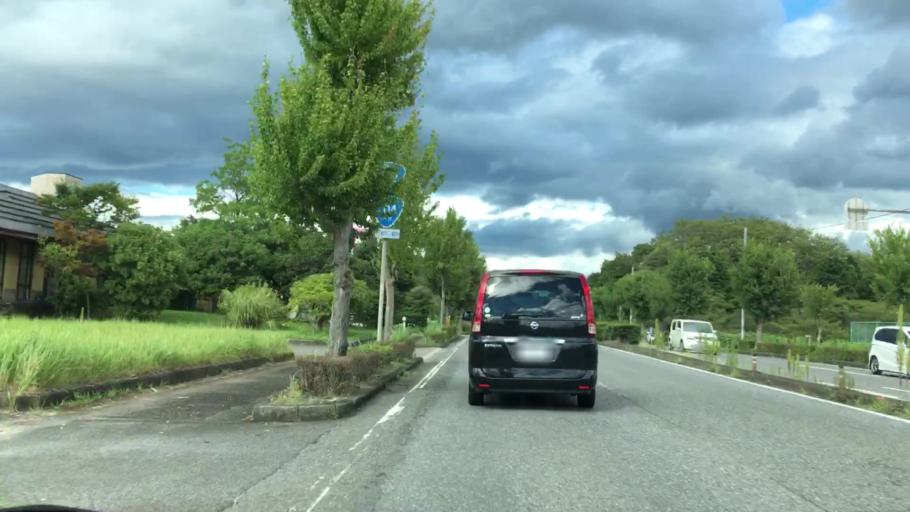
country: JP
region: Saga Prefecture
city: Imaricho-ko
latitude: 33.2657
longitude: 129.8650
